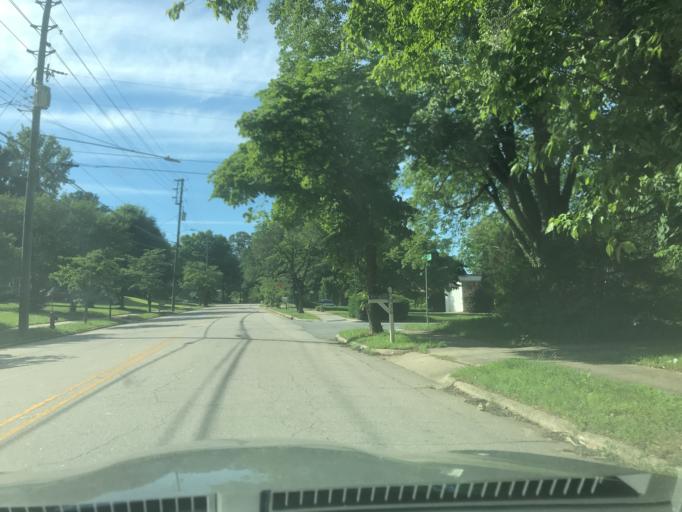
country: US
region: North Carolina
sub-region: Wake County
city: Raleigh
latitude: 35.8205
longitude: -78.5969
